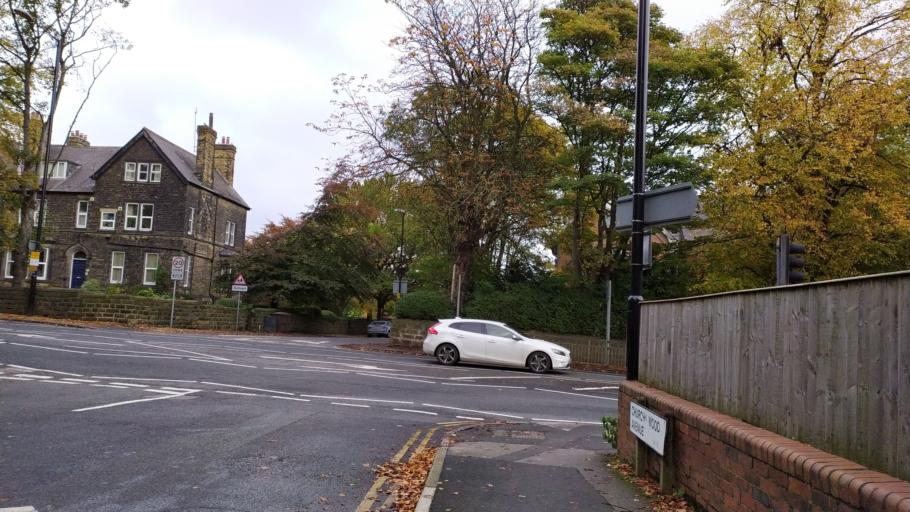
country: GB
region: England
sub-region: City and Borough of Leeds
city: Chapel Allerton
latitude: 53.8302
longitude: -1.5864
